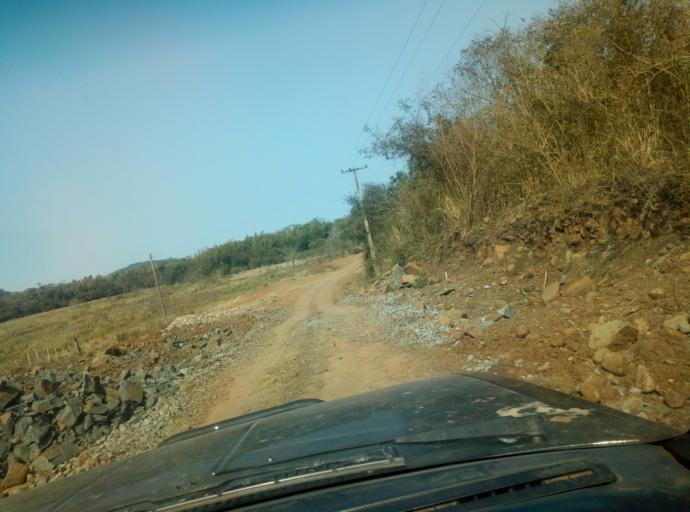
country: PY
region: Caaguazu
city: Coronel Oviedo
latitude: -25.3368
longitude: -56.3149
